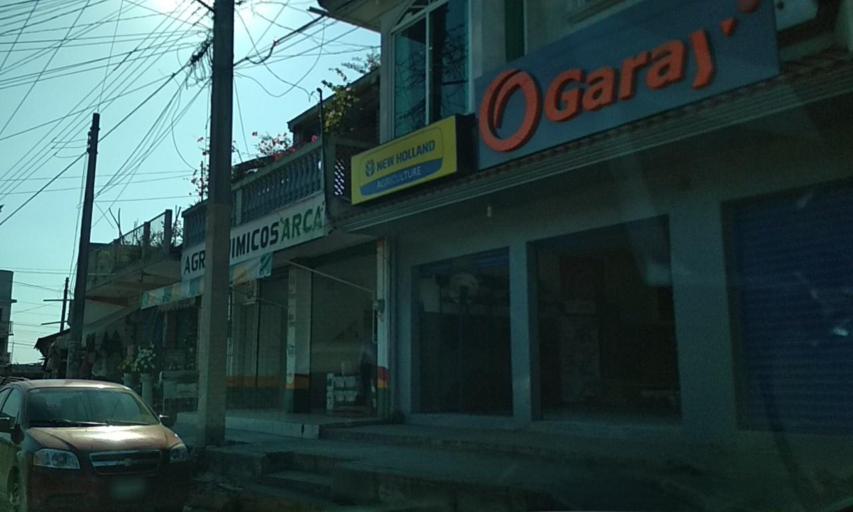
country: MX
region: Veracruz
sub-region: Papantla
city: El Chote
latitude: 20.4030
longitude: -97.3399
